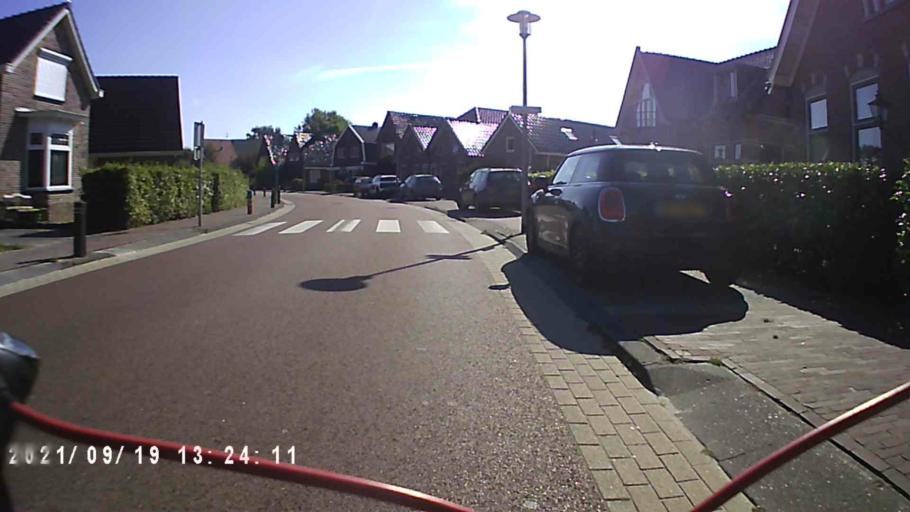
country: NL
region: Groningen
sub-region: Gemeente  Oldambt
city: Winschoten
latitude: 53.1558
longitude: 7.0064
